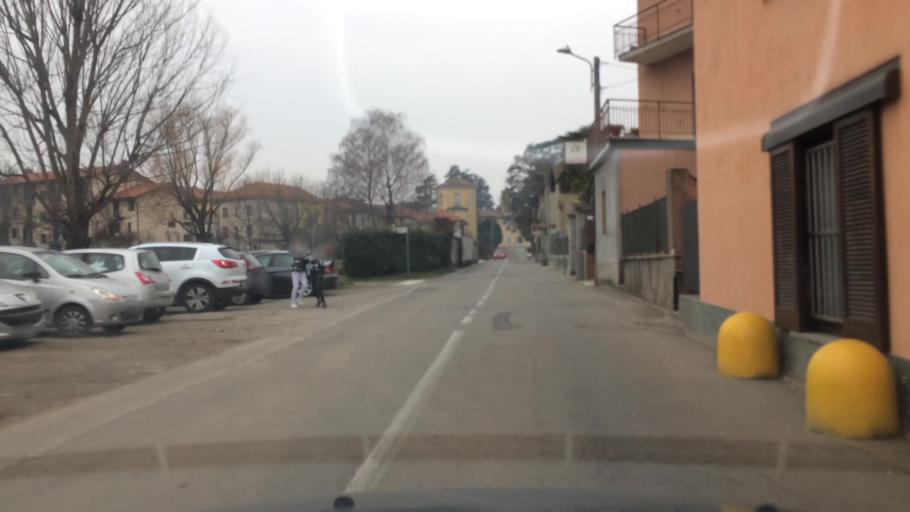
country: IT
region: Lombardy
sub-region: Provincia di Como
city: Novedrate
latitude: 45.6888
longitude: 9.1078
